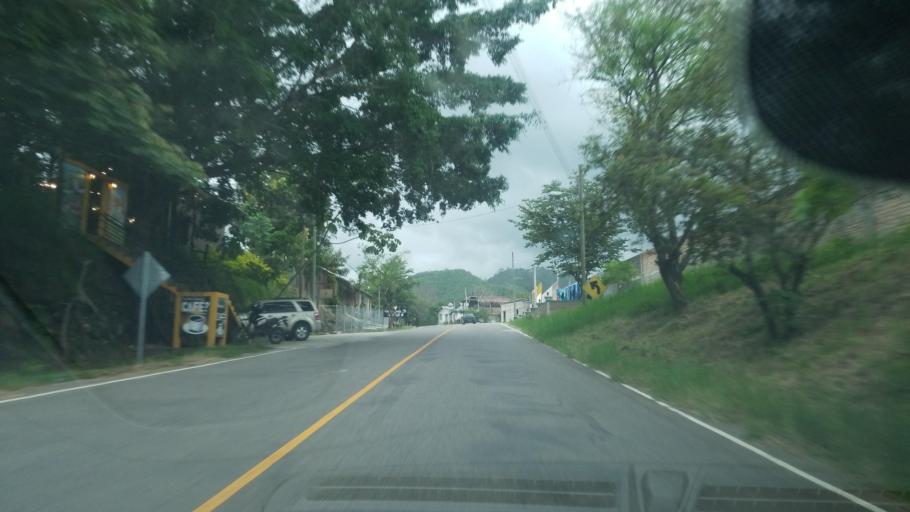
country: HN
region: Ocotepeque
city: Sinuapa
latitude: 14.5069
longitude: -89.2278
